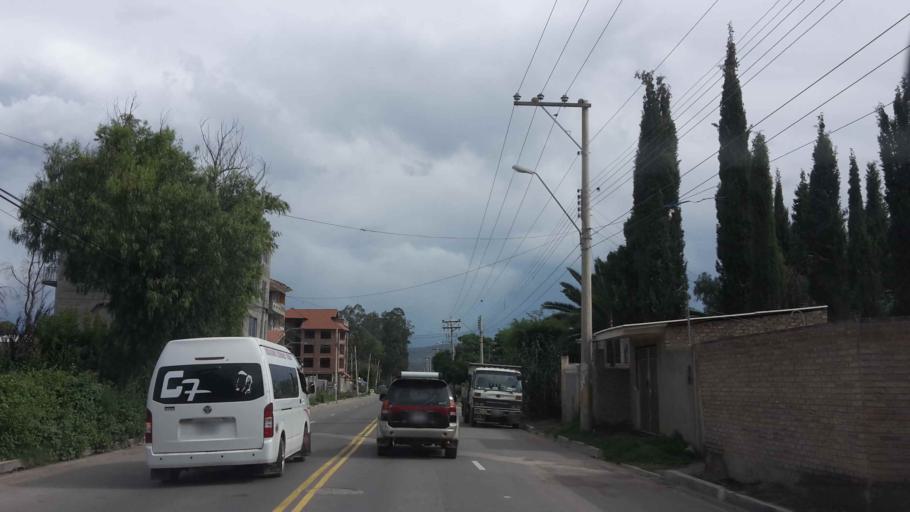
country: BO
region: Cochabamba
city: Cochabamba
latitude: -17.3761
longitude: -66.2519
